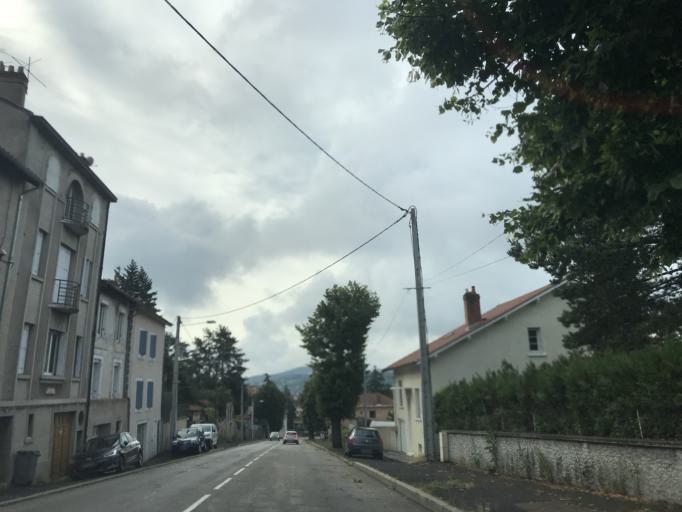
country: FR
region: Auvergne
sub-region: Departement de la Haute-Loire
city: Espaly-Saint-Marcel
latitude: 45.0538
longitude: 3.8671
